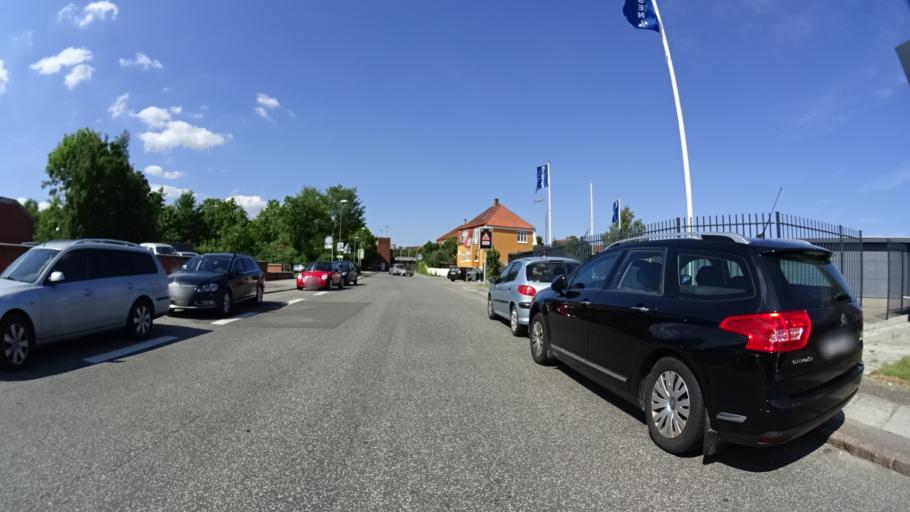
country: DK
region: Central Jutland
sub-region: Arhus Kommune
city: Arhus
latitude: 56.1510
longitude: 10.1656
